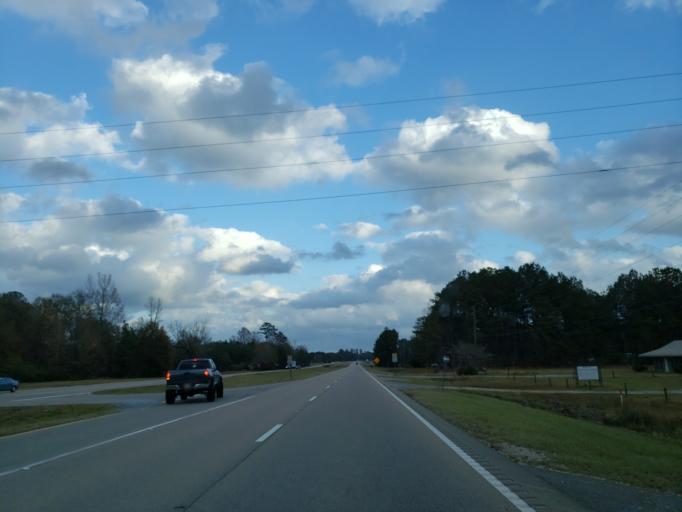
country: US
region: Mississippi
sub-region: Perry County
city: New Augusta
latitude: 31.2009
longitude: -89.0022
